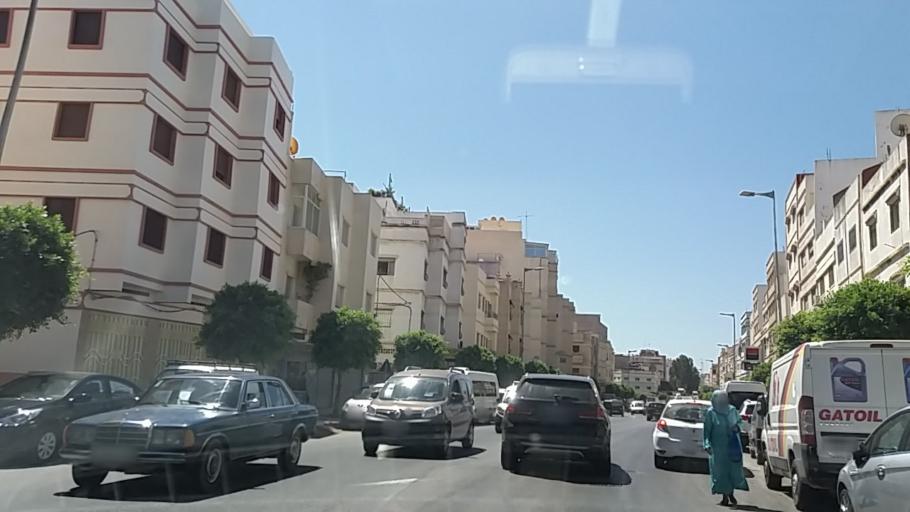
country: MA
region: Tanger-Tetouan
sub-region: Tanger-Assilah
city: Tangier
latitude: 35.7582
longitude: -5.8014
